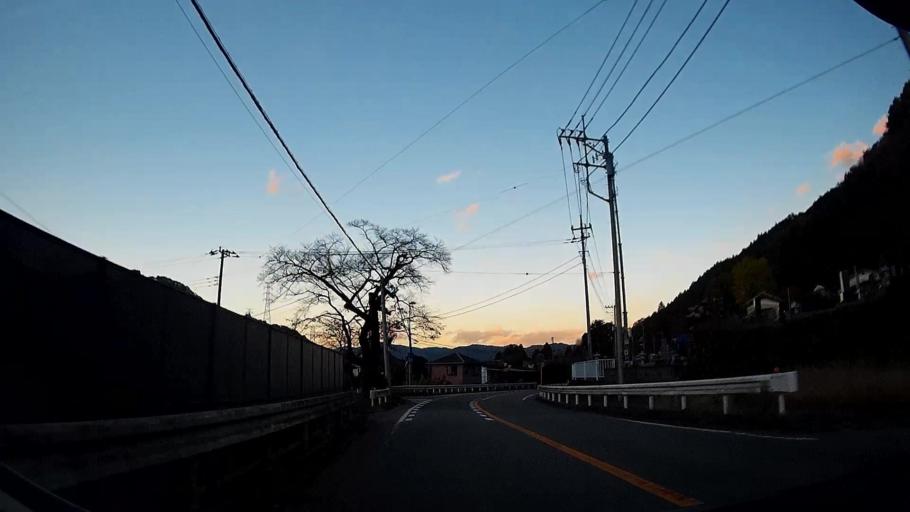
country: JP
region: Yamanashi
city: Uenohara
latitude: 35.5691
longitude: 139.2204
